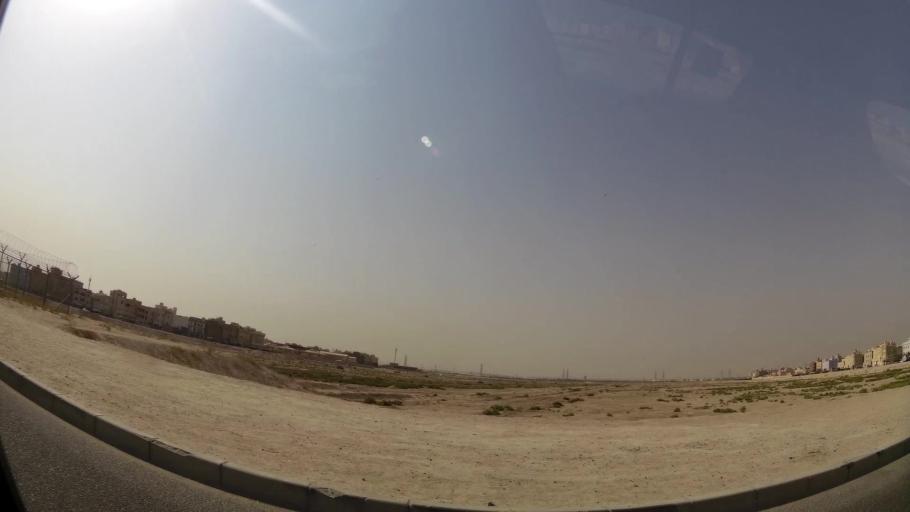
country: KW
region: Muhafazat al Jahra'
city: Al Jahra'
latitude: 29.3345
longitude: 47.7722
